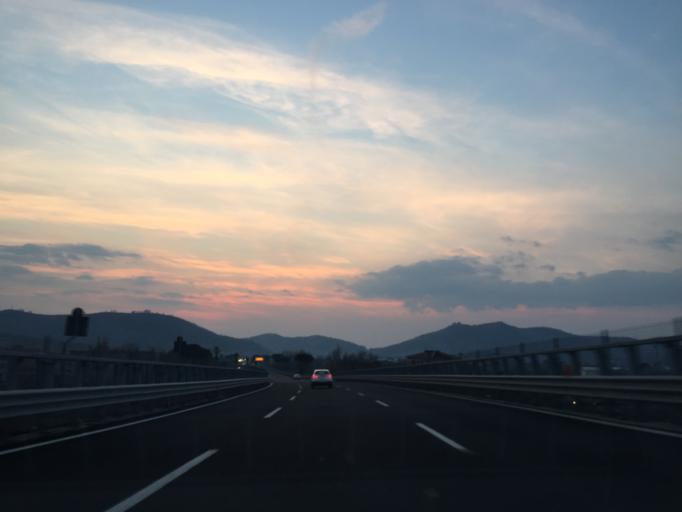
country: IT
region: Campania
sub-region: Provincia di Salerno
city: Roccapiemonte
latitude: 40.7680
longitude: 14.6994
